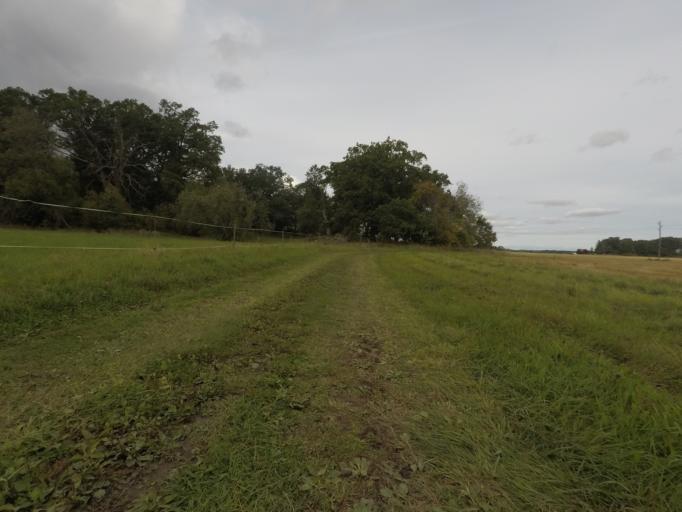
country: SE
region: Vaestmanland
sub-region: Kungsors Kommun
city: Kungsoer
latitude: 59.4550
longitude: 16.0501
